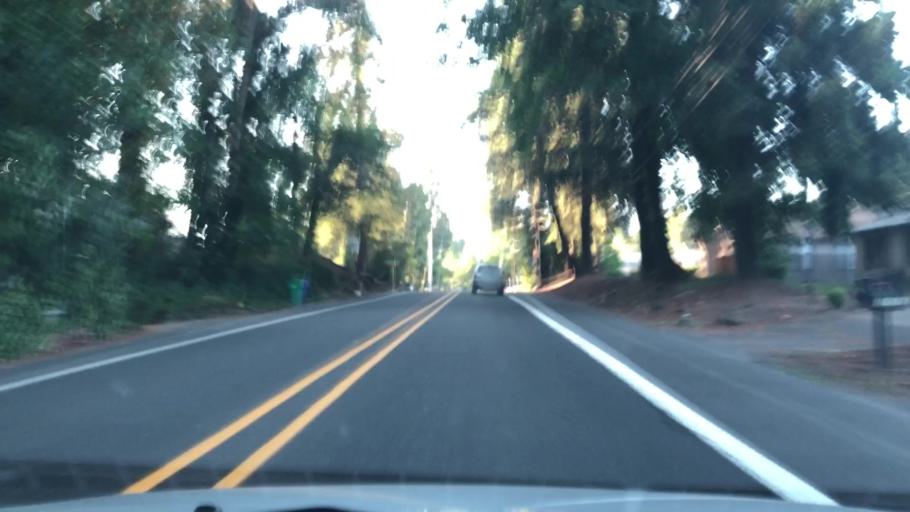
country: US
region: Oregon
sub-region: Clackamas County
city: Oak Grove
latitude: 45.4094
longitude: -122.6455
